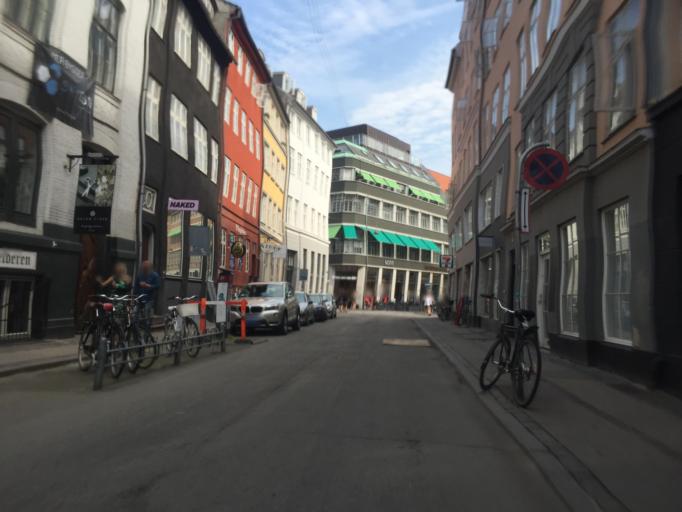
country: DK
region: Capital Region
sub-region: Kobenhavn
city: Copenhagen
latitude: 55.6811
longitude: 12.5793
